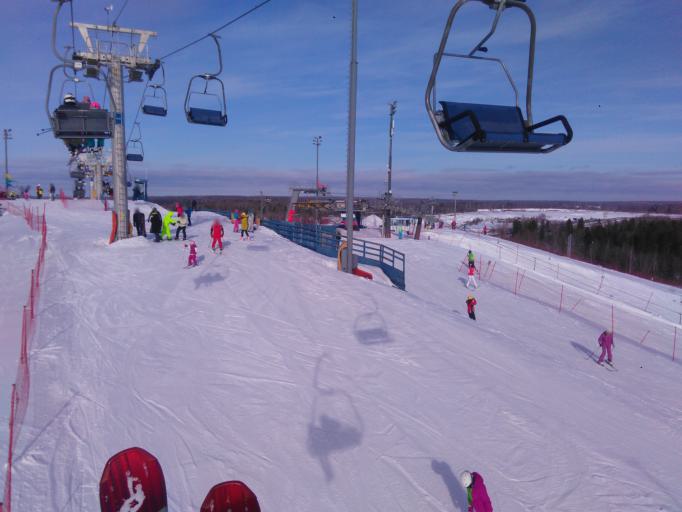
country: RU
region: Moskovskaya
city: Dedenevo
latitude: 56.2750
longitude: 37.5626
